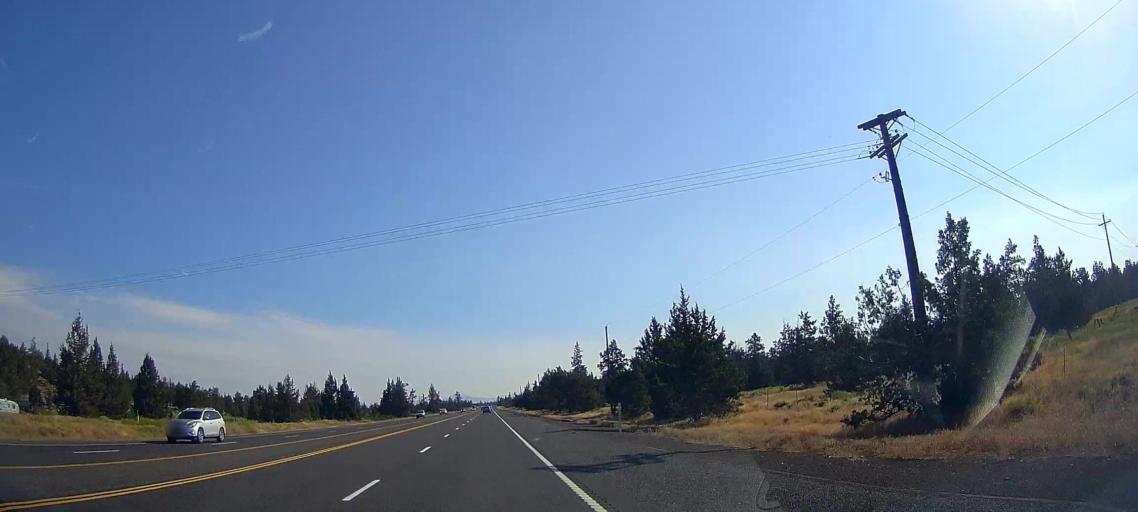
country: US
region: Oregon
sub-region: Deschutes County
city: Bend
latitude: 44.1674
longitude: -121.2542
